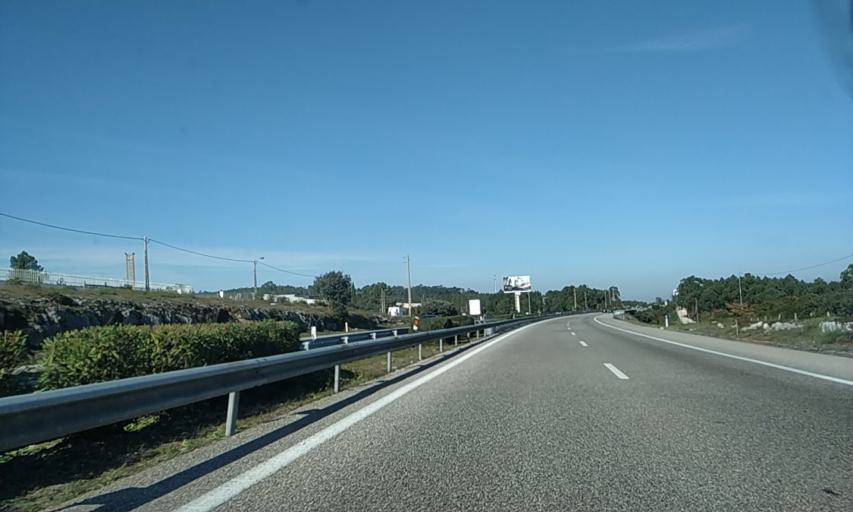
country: PT
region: Santarem
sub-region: Ourem
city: Fatima
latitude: 39.5658
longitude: -8.6518
